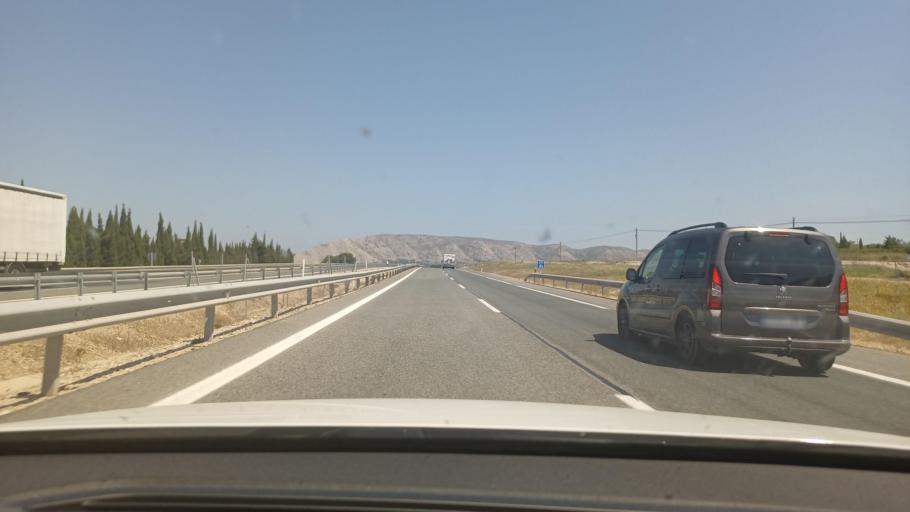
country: ES
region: Valencia
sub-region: Provincia de Alicante
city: Villena
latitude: 38.5911
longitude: -0.8439
